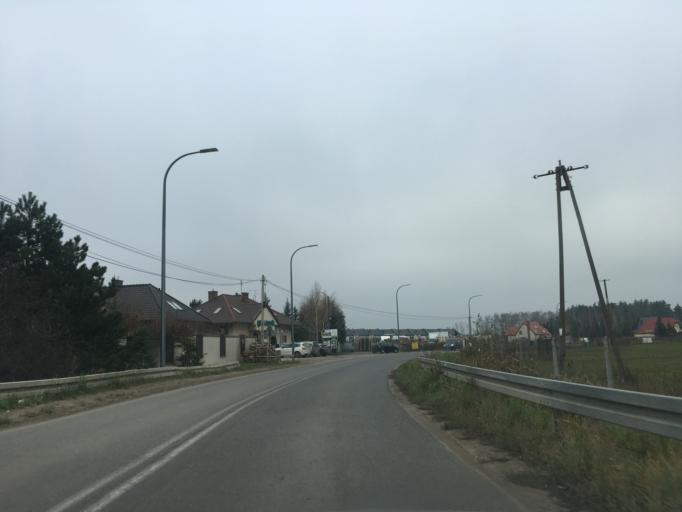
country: PL
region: Masovian Voivodeship
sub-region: Powiat piaseczynski
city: Lesznowola
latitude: 52.0721
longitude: 20.9666
